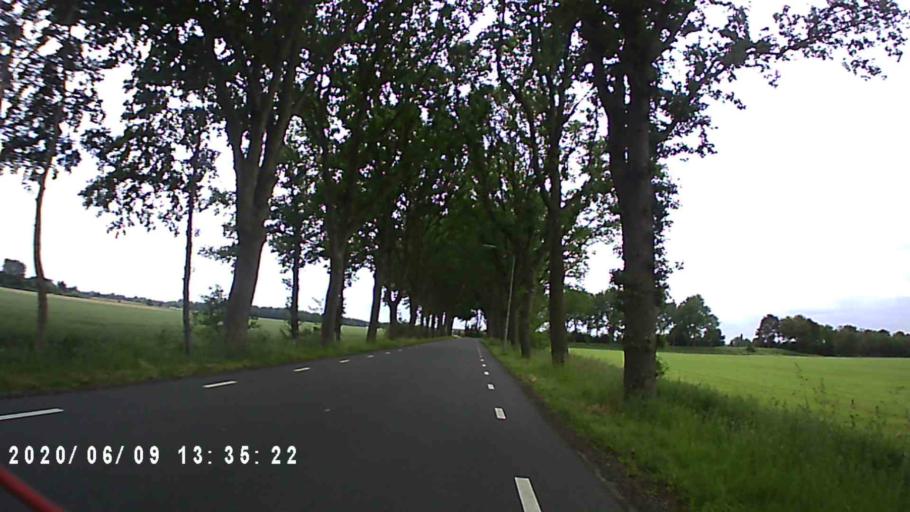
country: NL
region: Groningen
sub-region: Gemeente Haren
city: Haren
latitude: 53.2103
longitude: 6.6613
